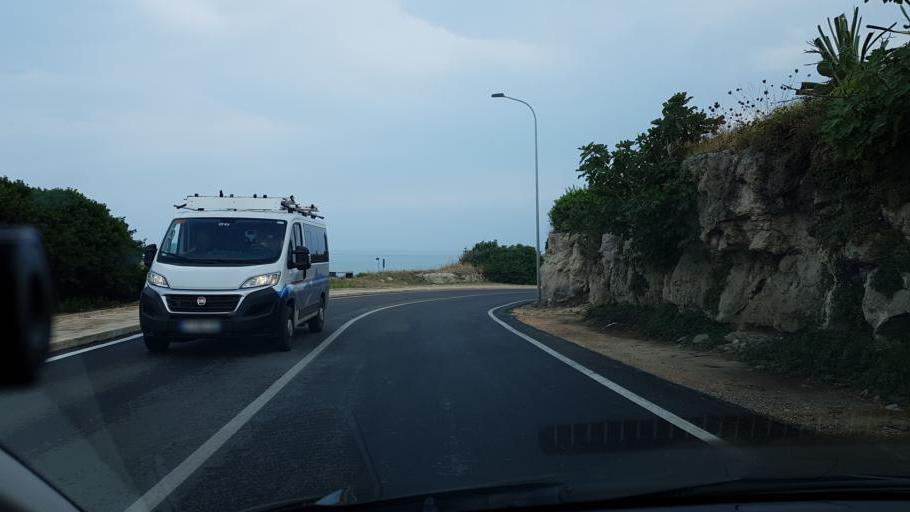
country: IT
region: Apulia
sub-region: Provincia di Bari
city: Monopoli
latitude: 40.9095
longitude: 17.3454
